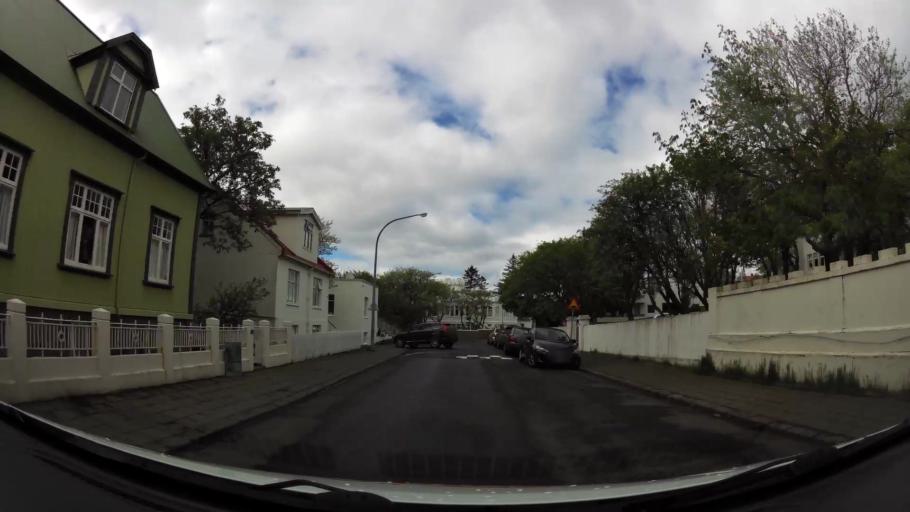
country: IS
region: Capital Region
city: Kopavogur
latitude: 64.1408
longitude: -21.9361
